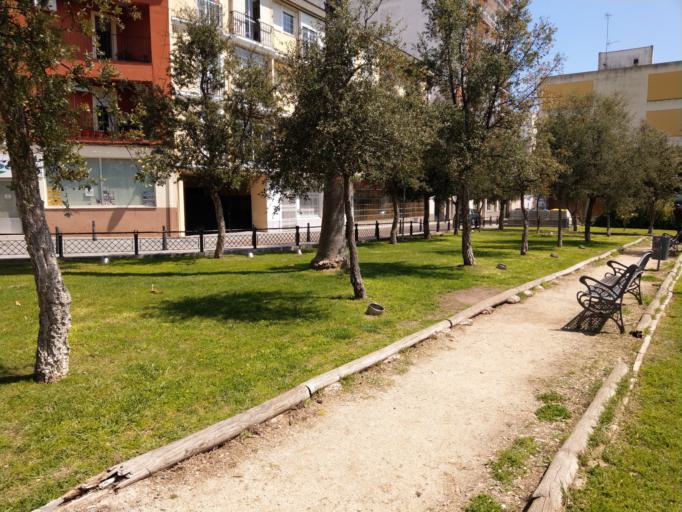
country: ES
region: Extremadura
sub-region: Provincia de Badajoz
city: Merida
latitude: 38.9144
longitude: -6.3458
